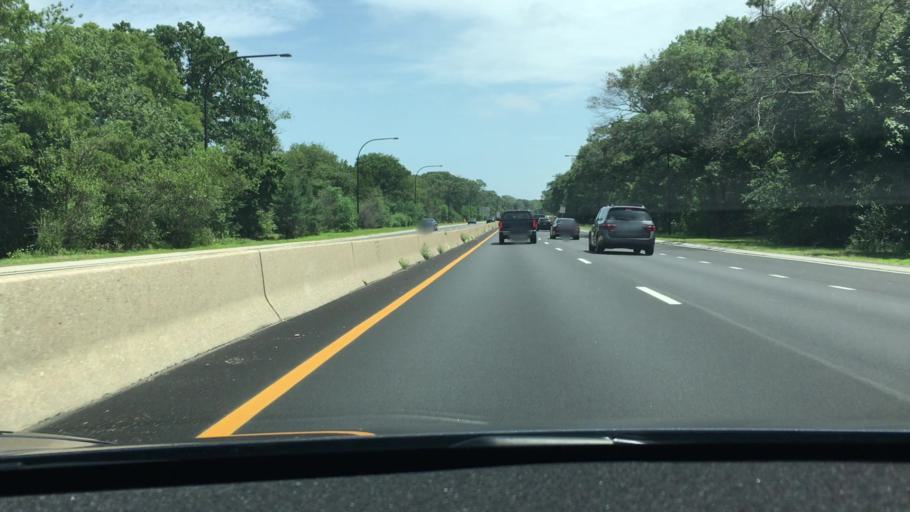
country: US
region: New York
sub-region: Nassau County
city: Levittown
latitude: 40.7200
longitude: -73.5347
